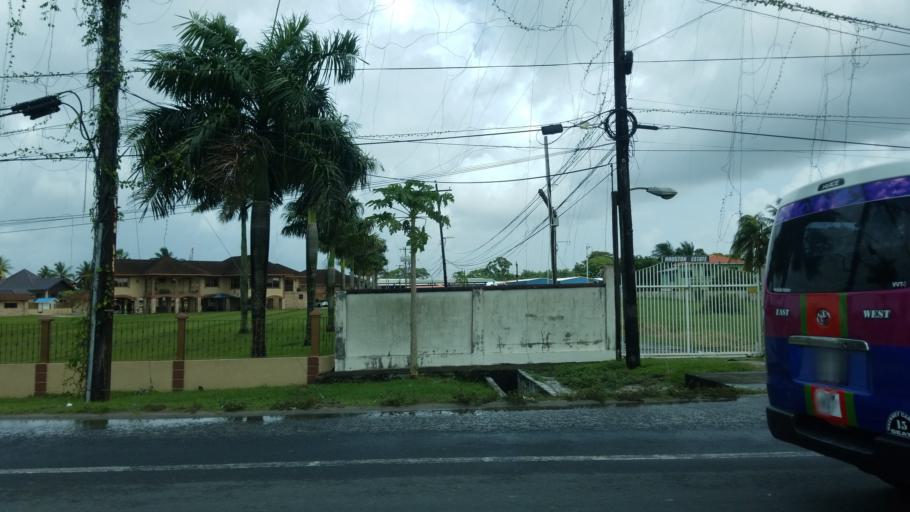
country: GY
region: Demerara-Mahaica
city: Georgetown
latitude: 6.7873
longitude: -58.1684
